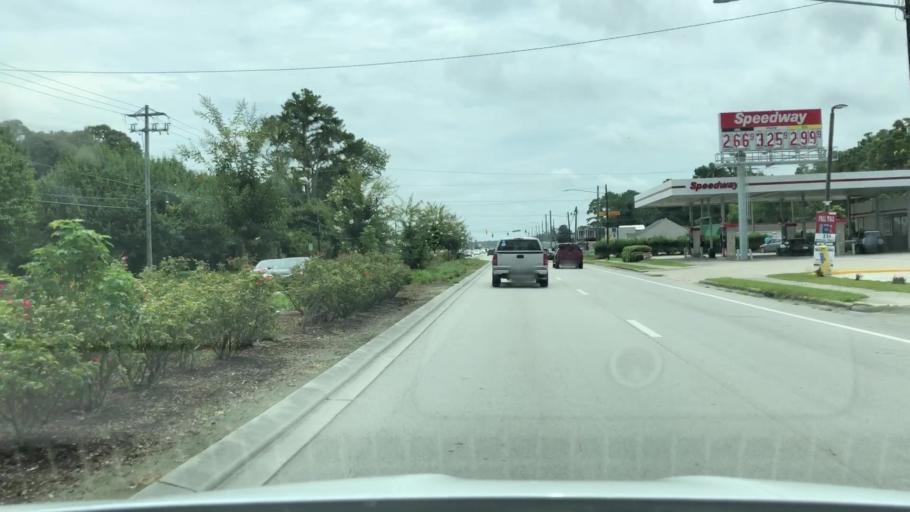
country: US
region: North Carolina
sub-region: Craven County
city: Havelock
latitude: 34.8726
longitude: -76.9023
